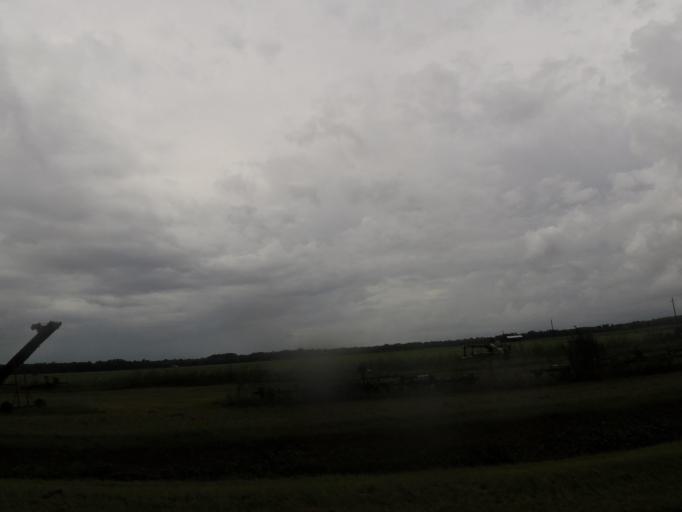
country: US
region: Florida
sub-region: Putnam County
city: East Palatka
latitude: 29.8451
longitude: -81.5479
